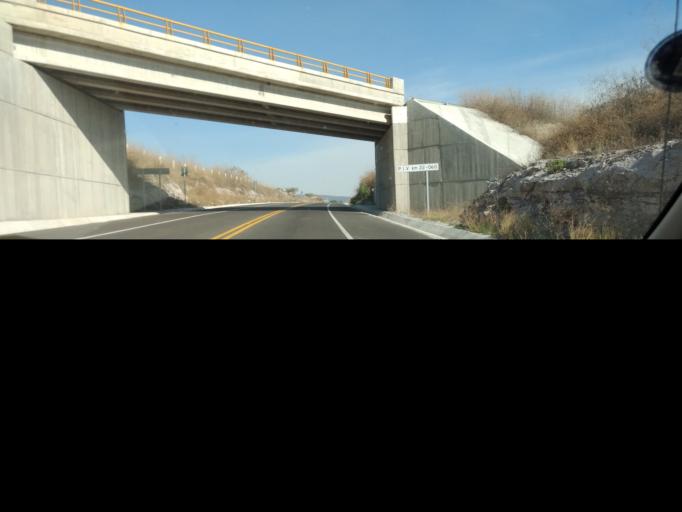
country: MX
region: Morelos
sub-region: Ayala
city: El Salitre
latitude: 18.6751
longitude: -98.9468
